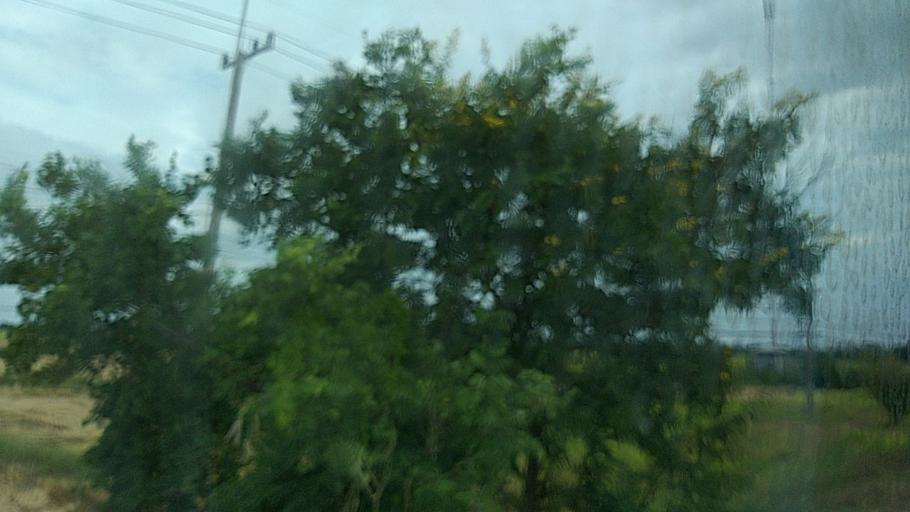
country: TH
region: Maha Sarakham
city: Maha Sarakham
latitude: 16.1507
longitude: 103.3859
